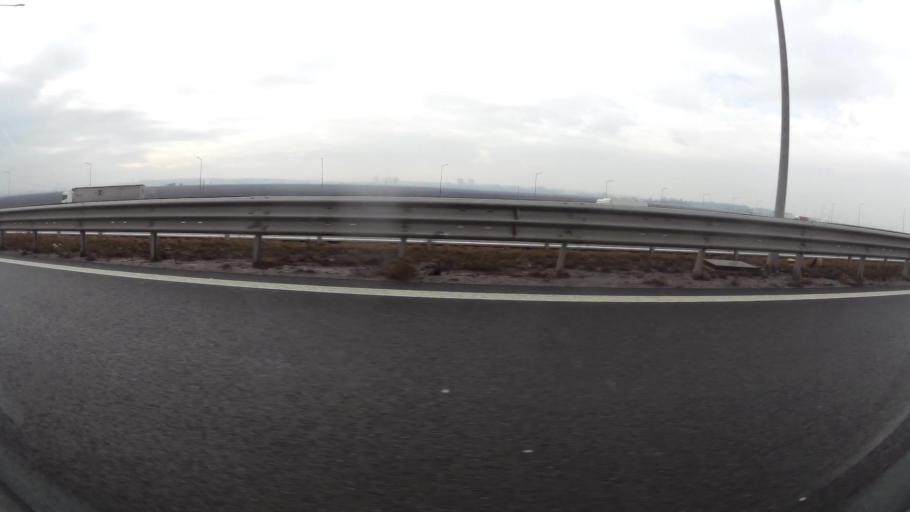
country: BG
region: Sofia-Capital
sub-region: Stolichna Obshtina
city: Sofia
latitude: 42.7680
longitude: 23.2899
